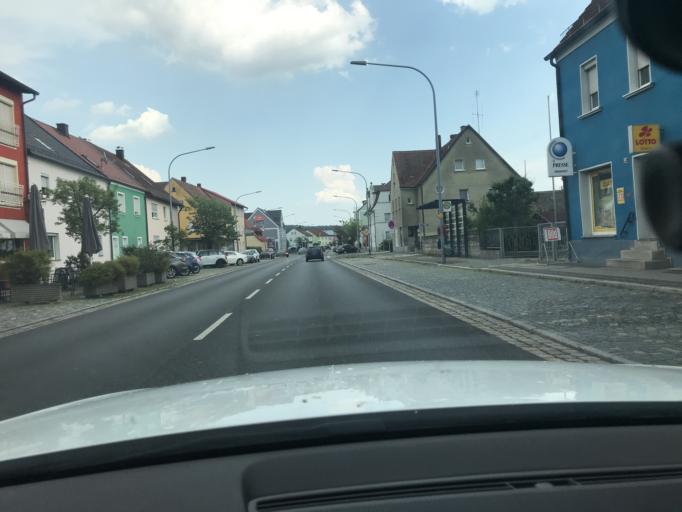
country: DE
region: Bavaria
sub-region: Upper Palatinate
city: Grafenwohr
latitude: 49.7190
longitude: 11.9075
